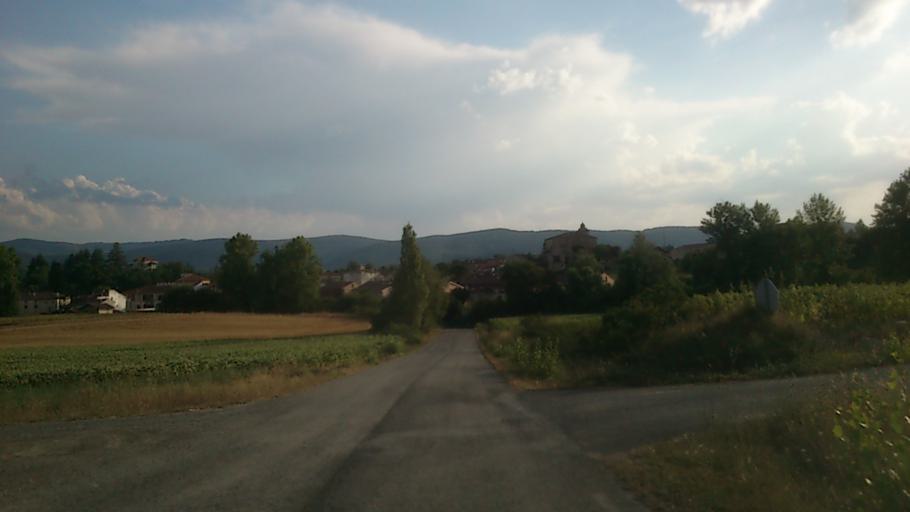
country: ES
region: Castille and Leon
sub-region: Provincia de Burgos
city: Frias
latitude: 42.7966
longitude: -3.2669
